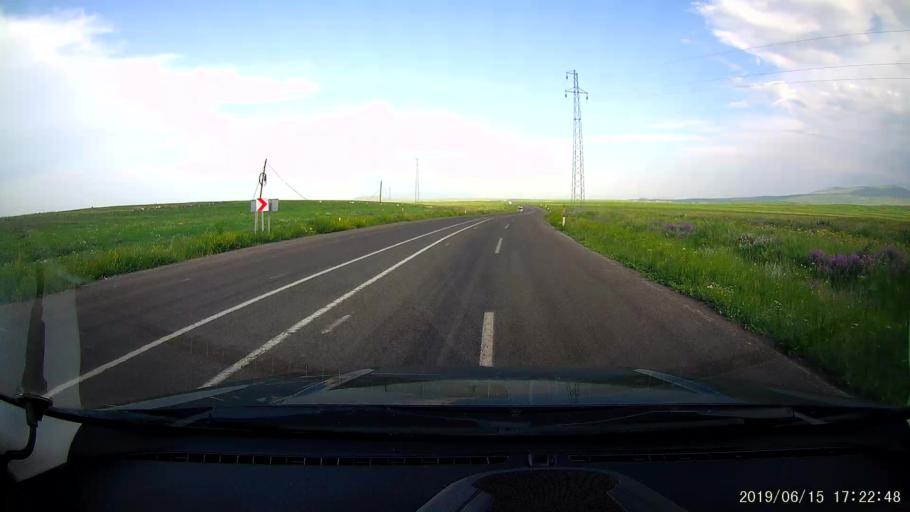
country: TR
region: Kars
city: Basgedikler
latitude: 40.6191
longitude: 43.3495
